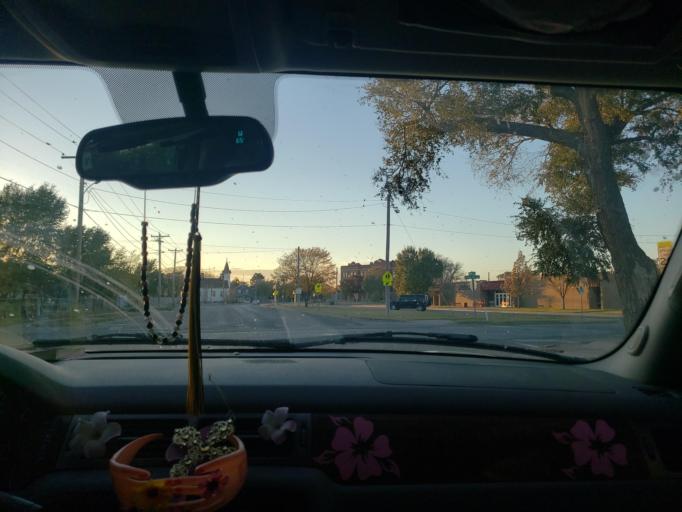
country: US
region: Kansas
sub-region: Finney County
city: Garden City
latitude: 37.9721
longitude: -100.8739
